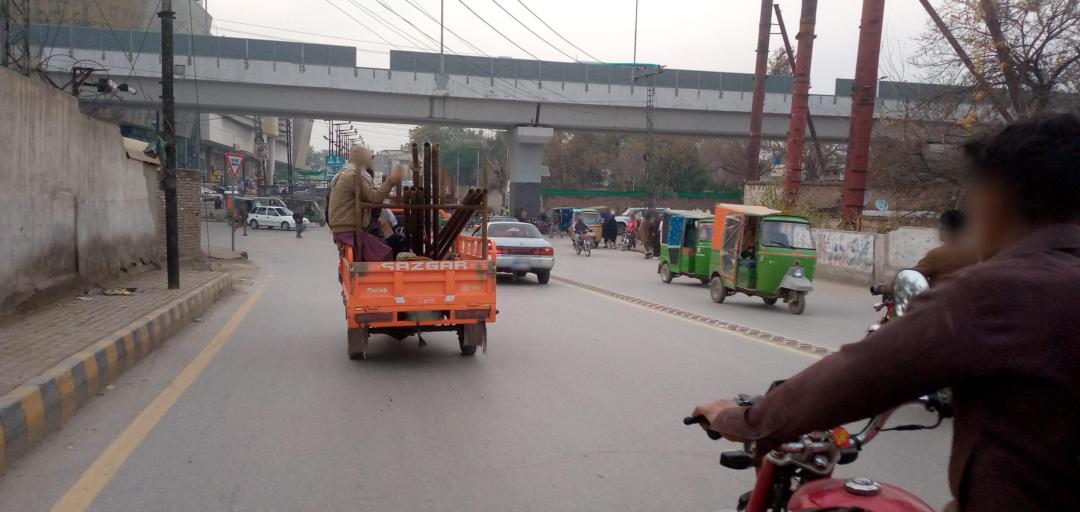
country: PK
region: Khyber Pakhtunkhwa
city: Peshawar
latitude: 34.0001
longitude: 71.5469
